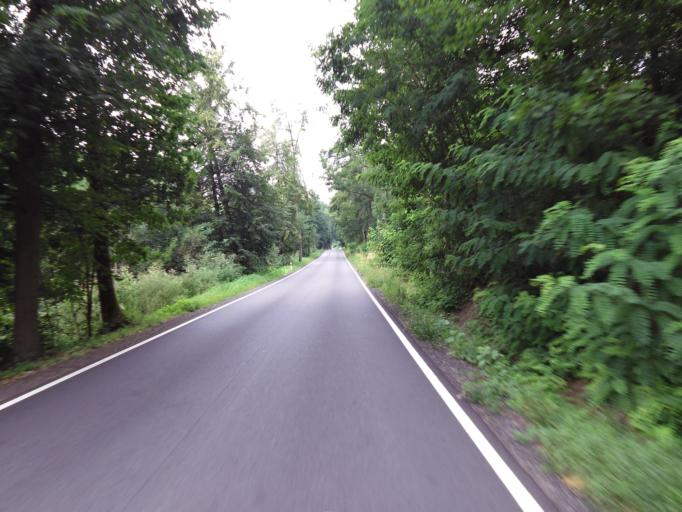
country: CZ
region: Central Bohemia
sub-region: Okres Benesov
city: Pysely
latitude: 49.8694
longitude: 14.6683
